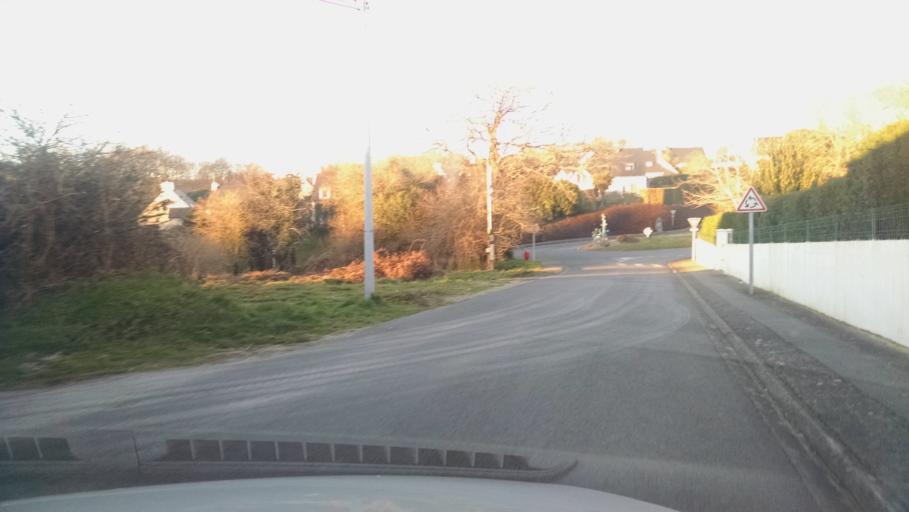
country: FR
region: Brittany
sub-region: Departement du Morbihan
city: Guidel-Plage
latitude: 47.7932
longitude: -3.5014
